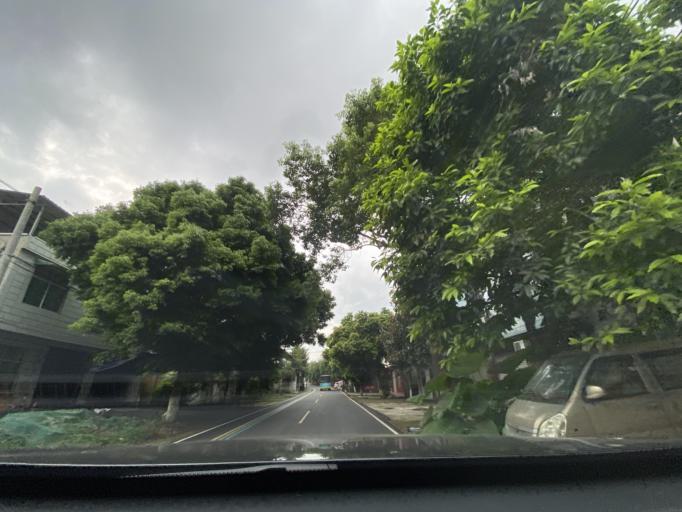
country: CN
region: Sichuan
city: Wujin
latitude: 30.4084
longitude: 103.9914
